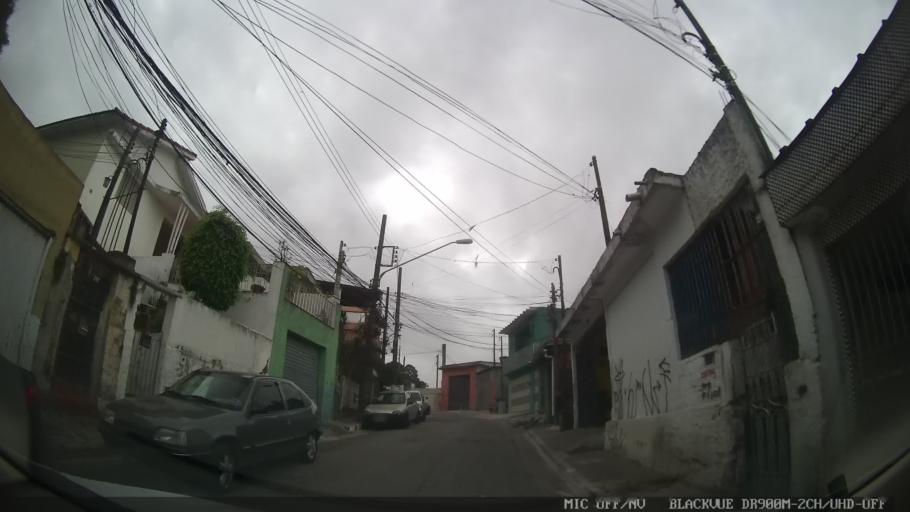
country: BR
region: Sao Paulo
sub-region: Sao Paulo
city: Sao Paulo
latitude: -23.4957
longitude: -46.6023
